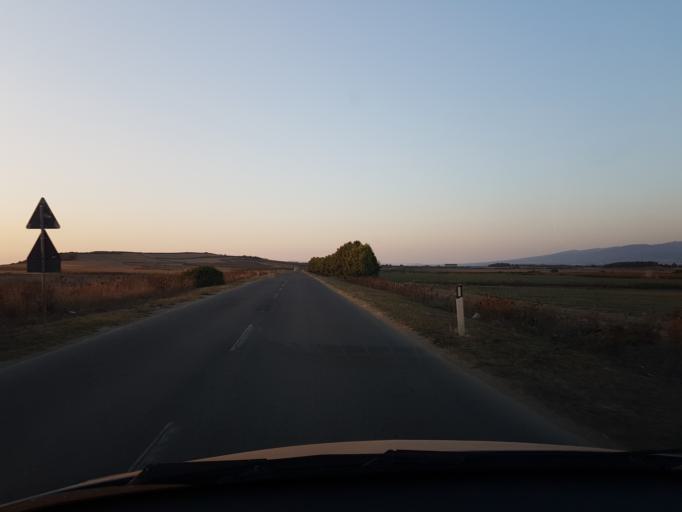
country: IT
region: Sardinia
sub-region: Provincia di Oristano
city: Nurachi
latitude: 39.9706
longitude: 8.4527
